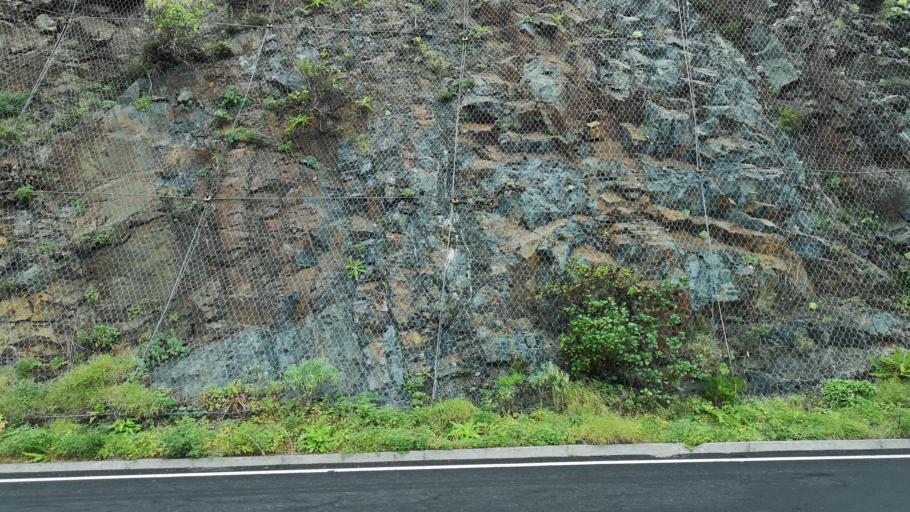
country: ES
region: Canary Islands
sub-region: Provincia de Santa Cruz de Tenerife
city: Agulo
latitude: 28.1879
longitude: -17.2156
